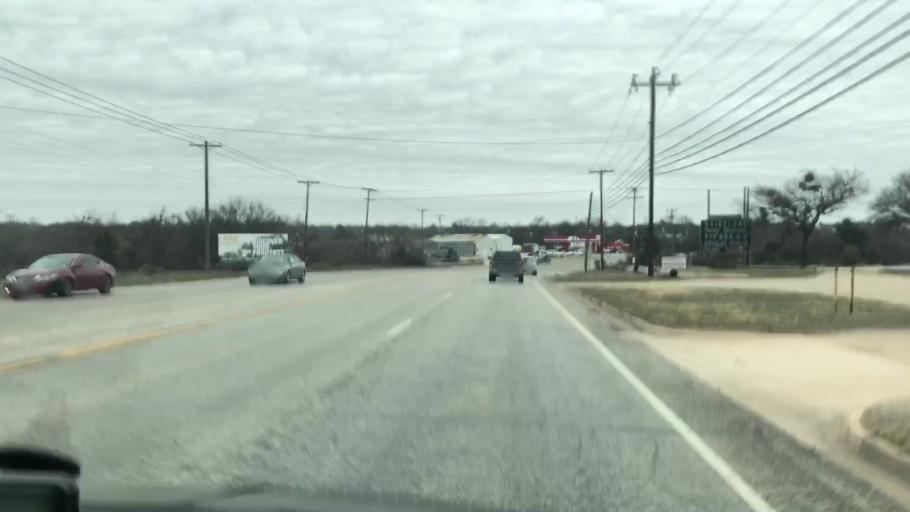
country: US
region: Texas
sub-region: Jack County
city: Jacksboro
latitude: 33.2105
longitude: -98.1576
